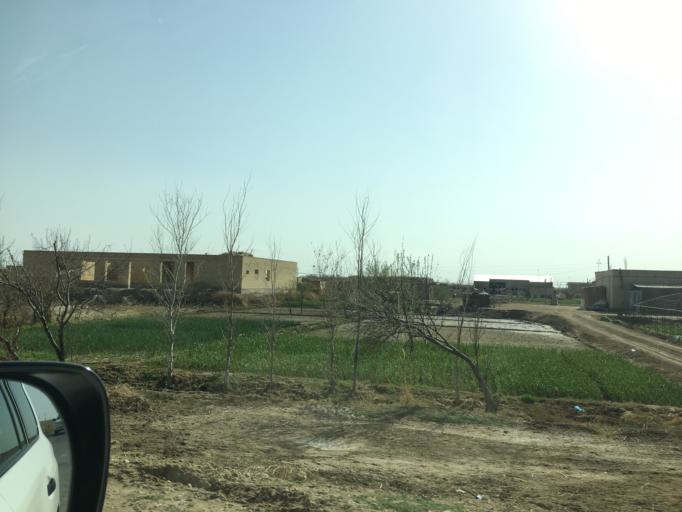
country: TM
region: Lebap
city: Farap
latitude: 39.2620
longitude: 63.4594
